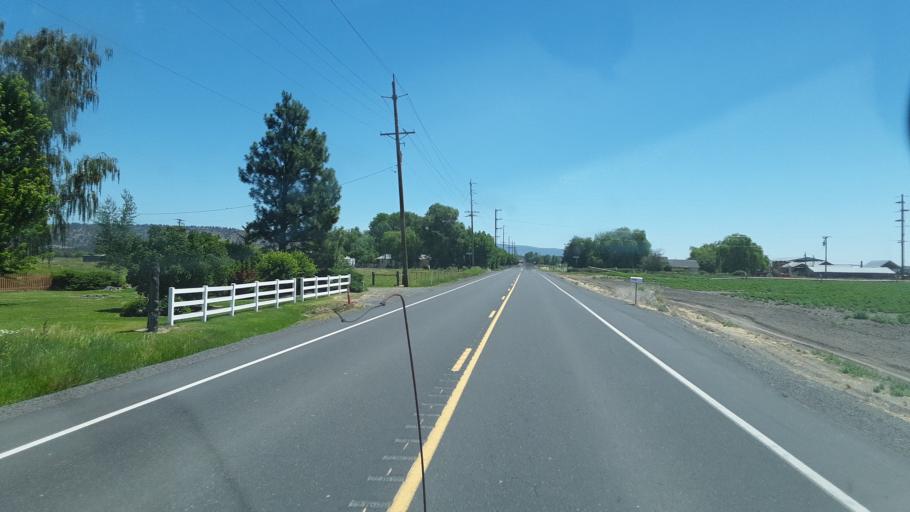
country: US
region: California
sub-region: Siskiyou County
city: Tulelake
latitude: 42.0240
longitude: -121.5630
